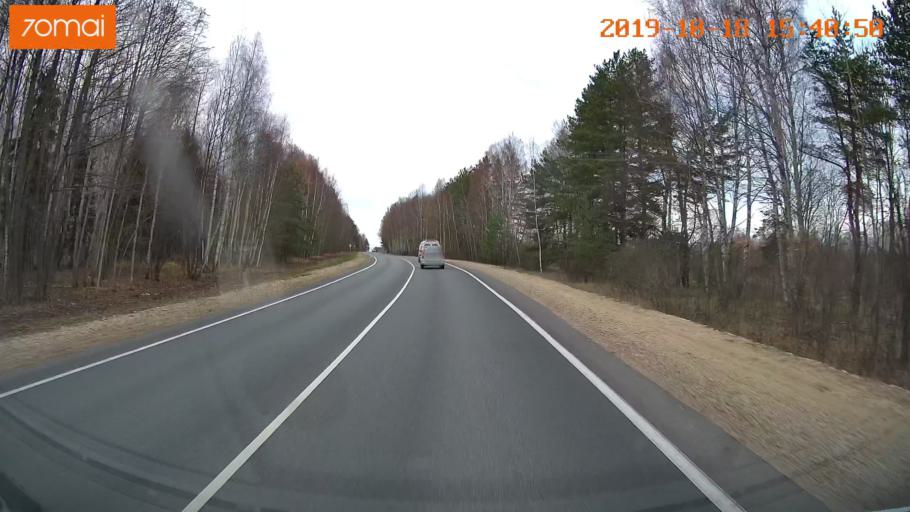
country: RU
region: Vladimir
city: Golovino
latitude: 55.9391
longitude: 40.5910
